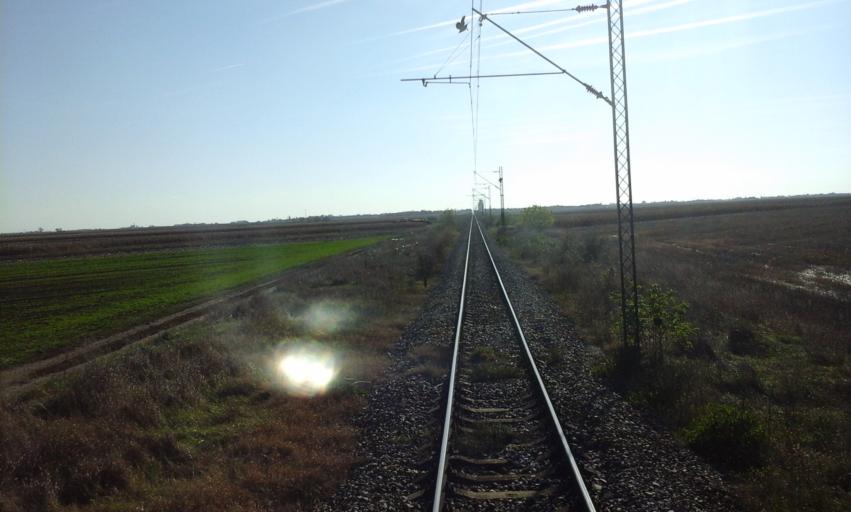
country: RS
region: Autonomna Pokrajina Vojvodina
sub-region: Severnobacki Okrug
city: Subotica
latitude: 45.9704
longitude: 19.6730
